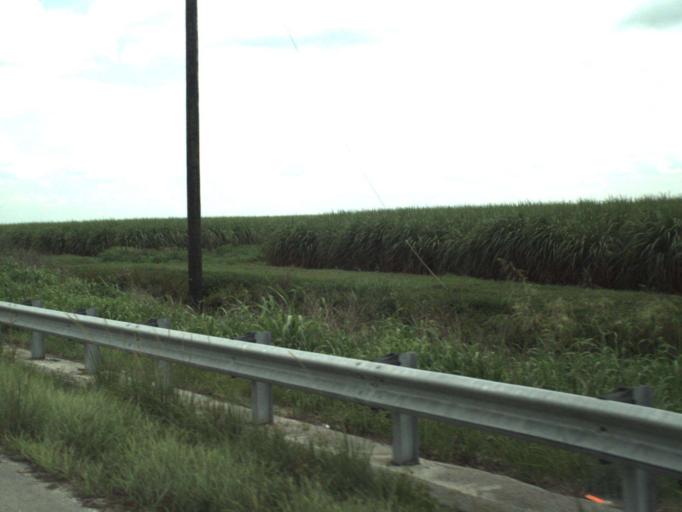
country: US
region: Florida
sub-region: Palm Beach County
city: Pahokee
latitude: 26.7605
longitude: -80.4943
